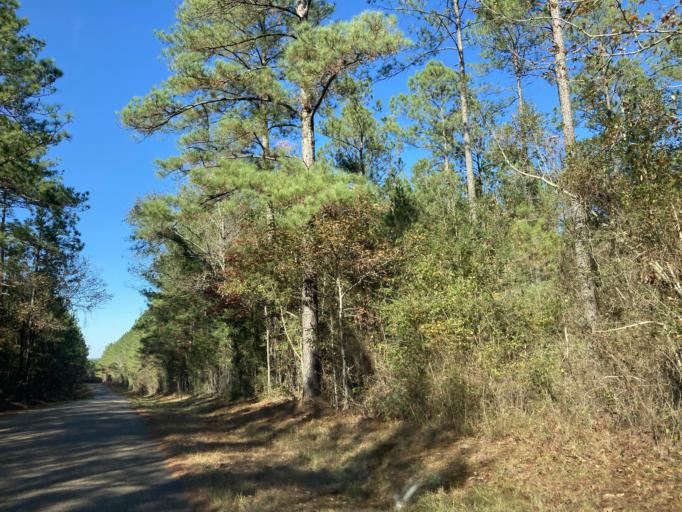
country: US
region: Mississippi
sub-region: Lamar County
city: Sumrall
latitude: 31.3099
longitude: -89.6074
